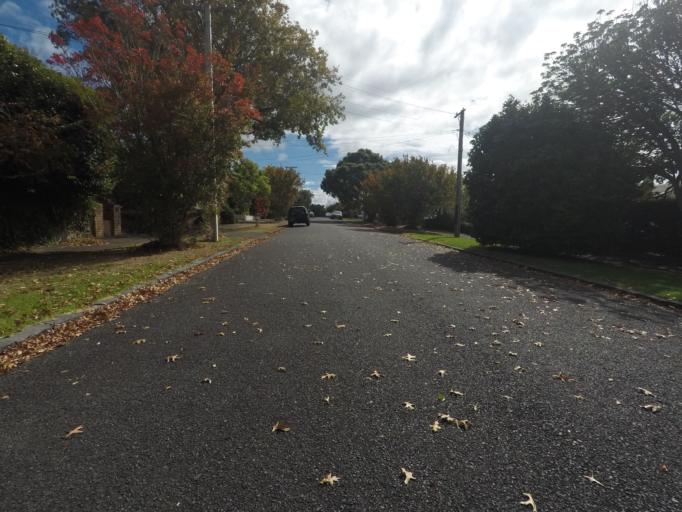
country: NZ
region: Auckland
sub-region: Auckland
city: Auckland
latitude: -36.8810
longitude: 174.7212
